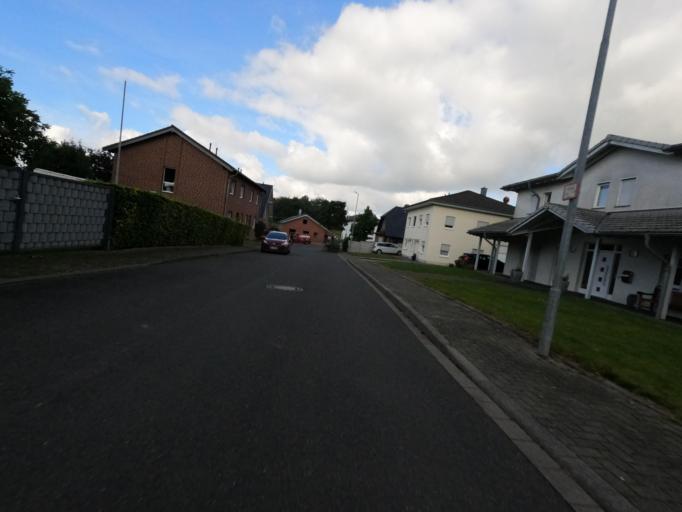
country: DE
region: North Rhine-Westphalia
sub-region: Regierungsbezirk Koln
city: Linnich
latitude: 51.0014
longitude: 6.2831
